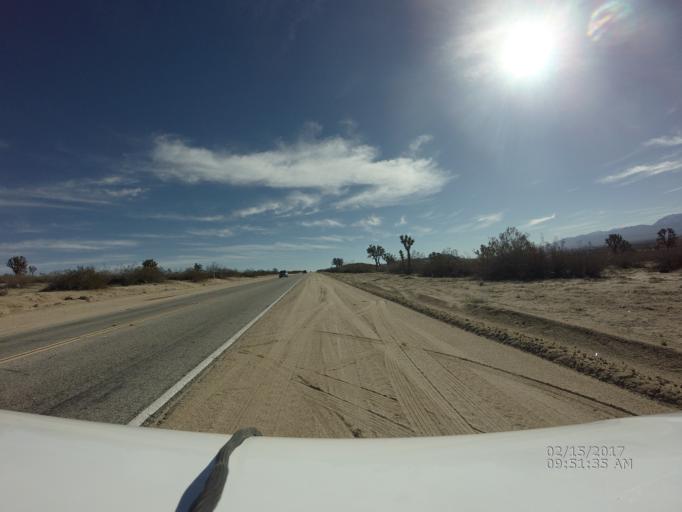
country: US
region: California
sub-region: Los Angeles County
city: Lake Los Angeles
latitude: 34.6166
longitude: -117.9100
